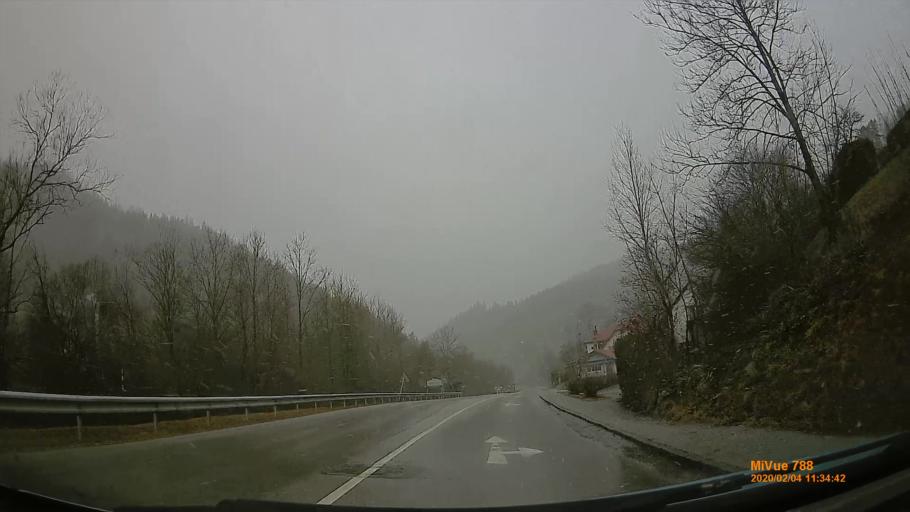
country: AT
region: Styria
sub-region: Politischer Bezirk Bruck-Muerzzuschlag
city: Neuberg an der Muerz
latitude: 47.6706
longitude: 15.5711
